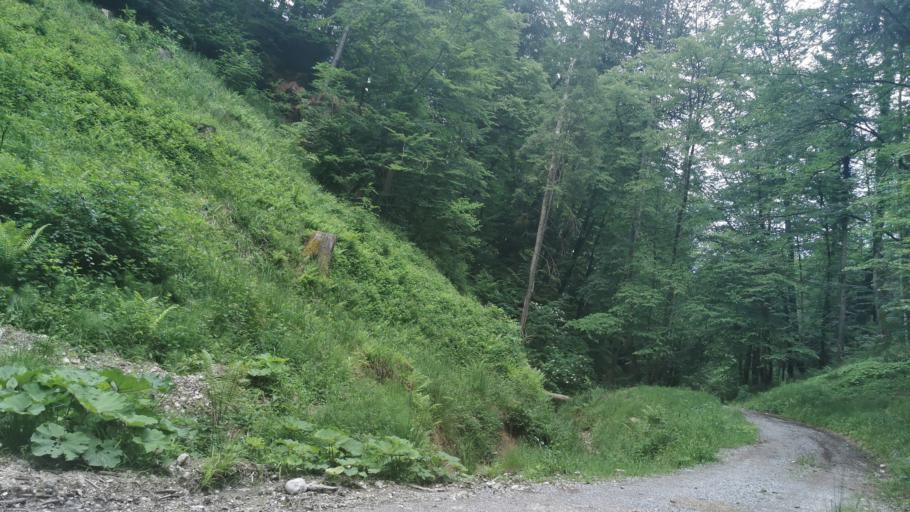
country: AT
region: Salzburg
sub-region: Politischer Bezirk Salzburg-Umgebung
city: Grodig
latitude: 47.7480
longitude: 12.9780
